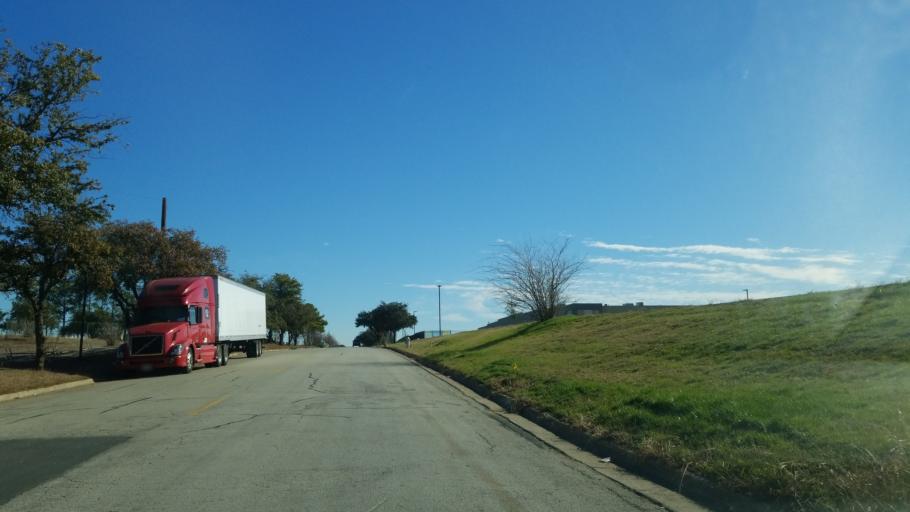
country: US
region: Texas
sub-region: Tarrant County
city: Arlington
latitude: 32.7463
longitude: -97.0616
